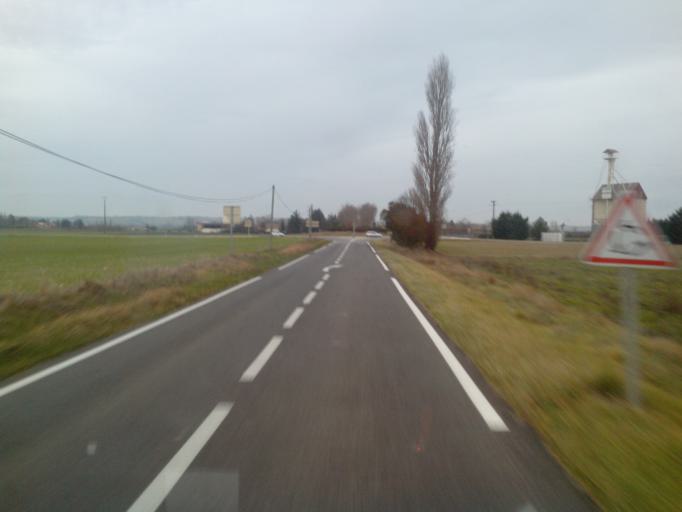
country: FR
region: Midi-Pyrenees
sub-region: Departement de l'Ariege
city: Mazeres
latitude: 43.2333
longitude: 1.6544
